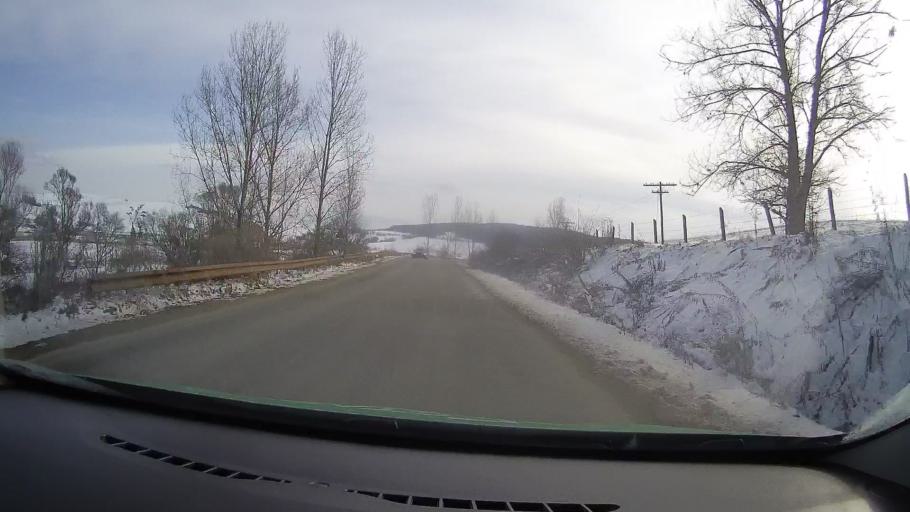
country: RO
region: Sibiu
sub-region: Oras Agnita
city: Ruja
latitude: 46.0008
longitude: 24.6726
